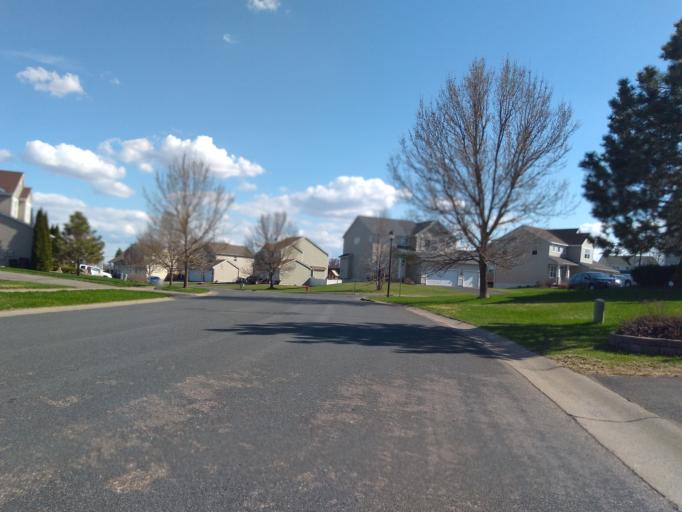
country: US
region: Minnesota
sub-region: Dakota County
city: Rosemount
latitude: 44.7411
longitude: -93.1074
